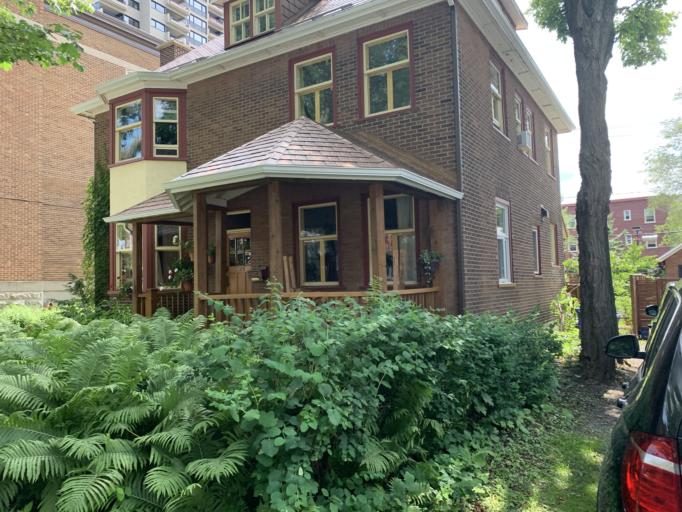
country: CA
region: Quebec
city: Quebec
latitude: 46.8005
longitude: -71.2292
